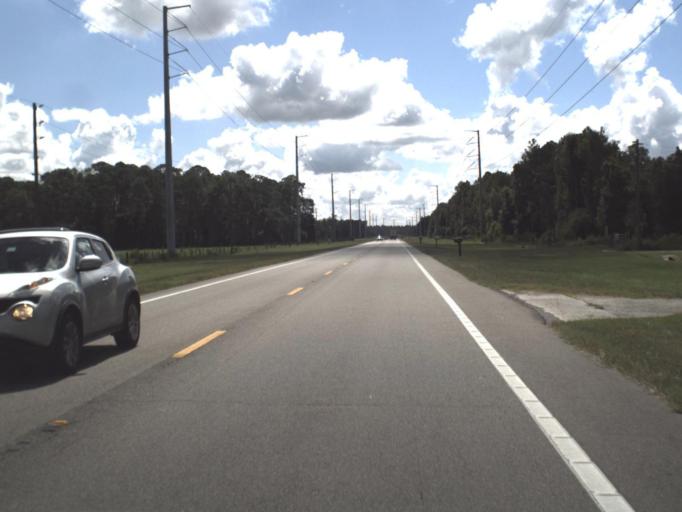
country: US
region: Florida
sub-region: Pasco County
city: Zephyrhills North
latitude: 28.2549
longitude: -82.0679
